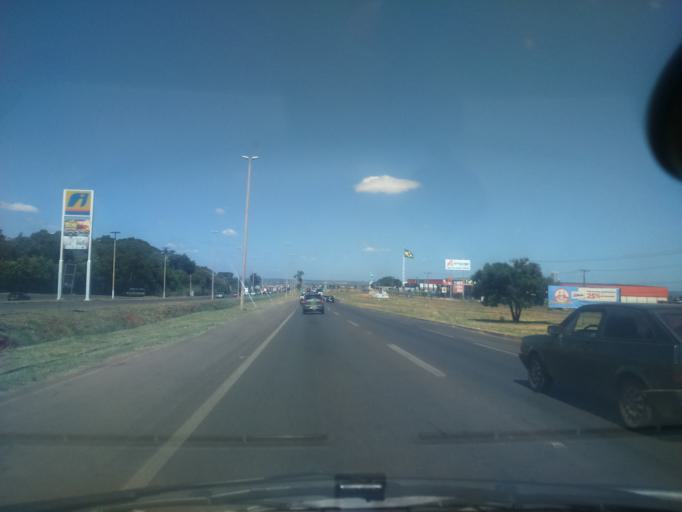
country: BR
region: Goias
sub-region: Luziania
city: Luziania
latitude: -16.0902
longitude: -47.9841
